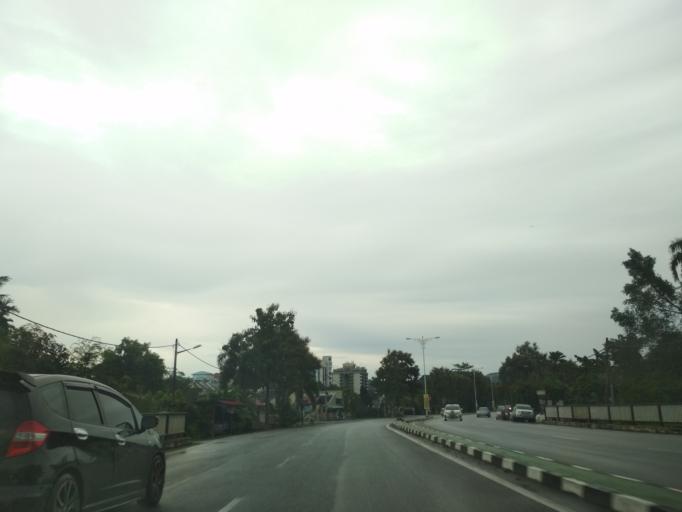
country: MY
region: Perlis
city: Kangar
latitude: 6.4408
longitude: 100.2075
